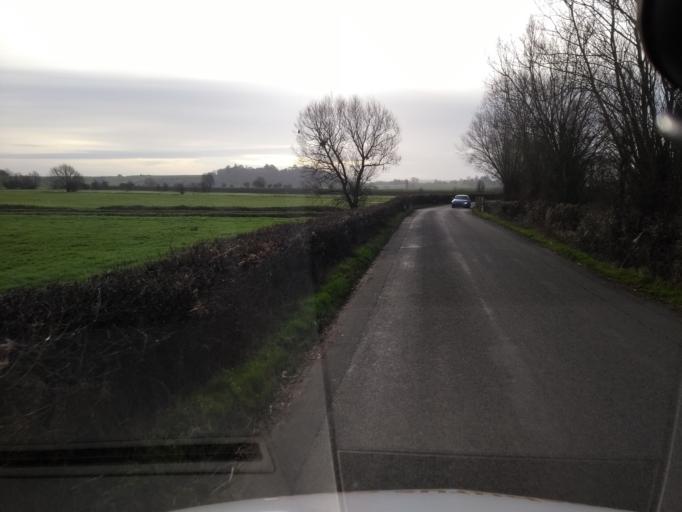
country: GB
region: England
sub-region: Somerset
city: Creech Saint Michael
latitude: 51.0400
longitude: -2.9770
